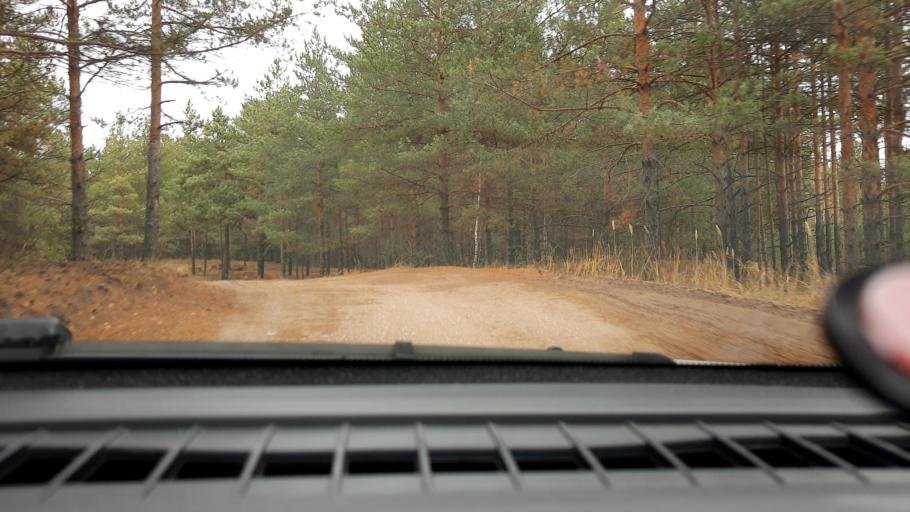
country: RU
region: Nizjnij Novgorod
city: Lukino
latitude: 56.3860
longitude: 43.6481
